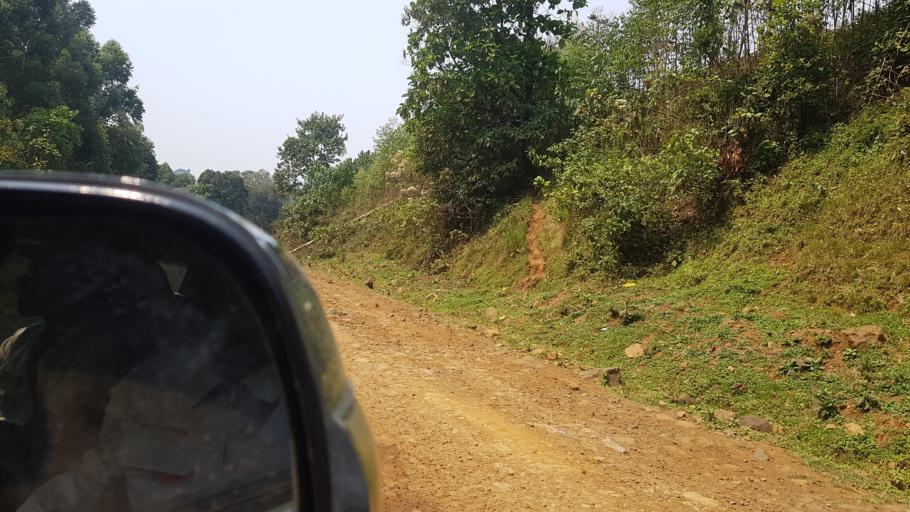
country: ET
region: Oromiya
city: Gore
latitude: 7.7977
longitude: 35.4571
